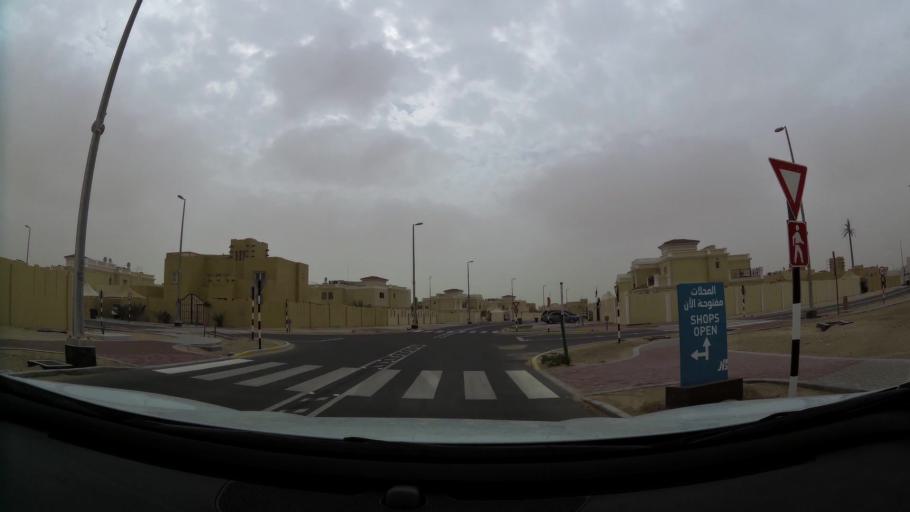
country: AE
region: Abu Dhabi
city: Abu Dhabi
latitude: 24.4532
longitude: 54.7366
